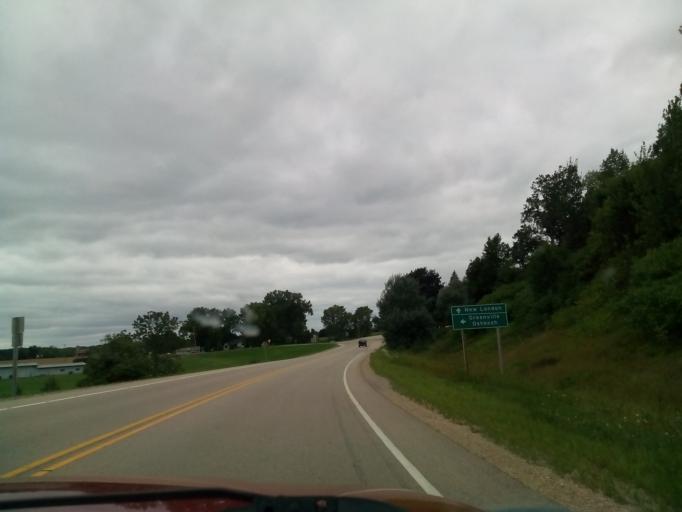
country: US
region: Wisconsin
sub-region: Outagamie County
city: Hortonville
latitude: 44.3801
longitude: -88.5796
